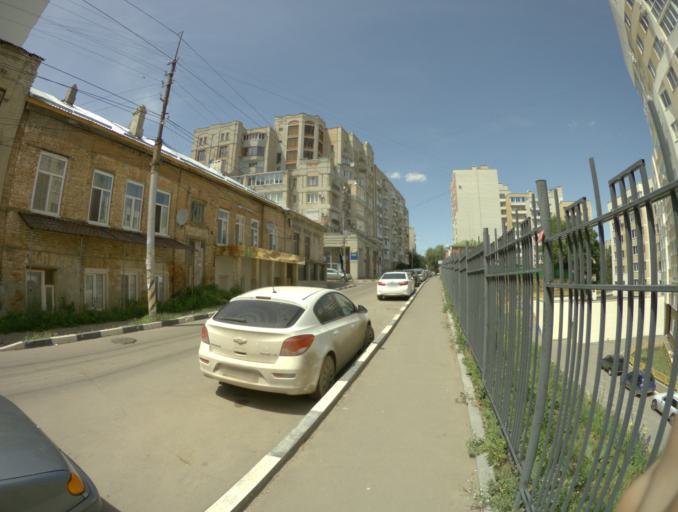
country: RU
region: Saratov
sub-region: Saratovskiy Rayon
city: Saratov
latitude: 51.5293
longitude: 46.0578
